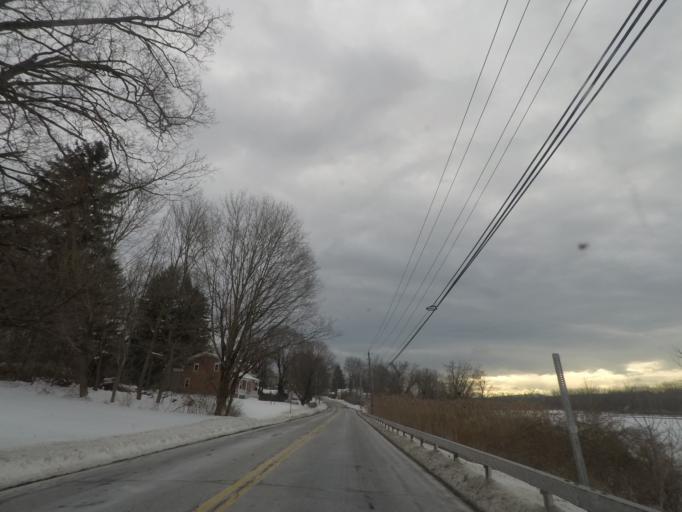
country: US
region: New York
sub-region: Rensselaer County
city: Castleton-on-Hudson
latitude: 42.4836
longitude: -73.7698
